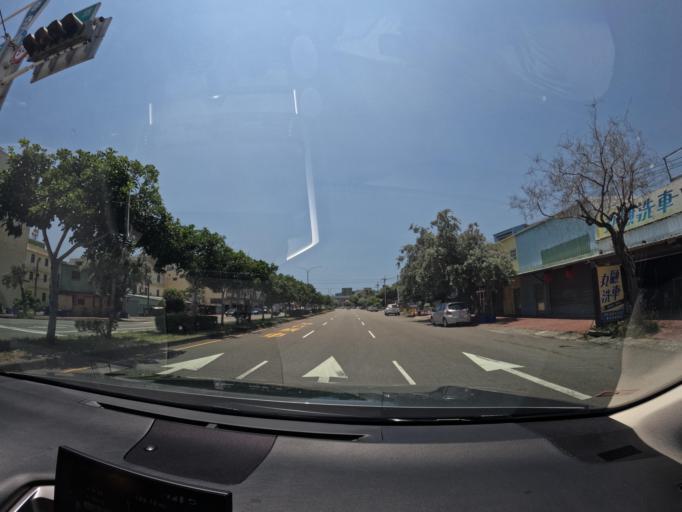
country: TW
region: Taiwan
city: Fengyuan
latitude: 24.2565
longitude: 120.5430
